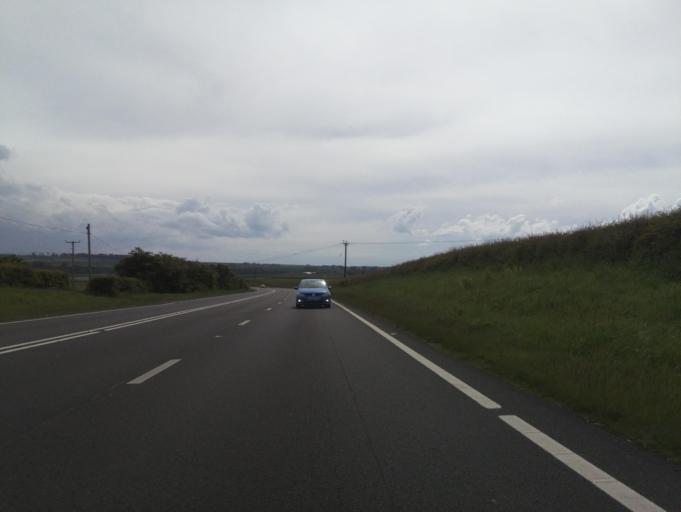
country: GB
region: England
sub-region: Northumberland
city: Berwick-Upon-Tweed
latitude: 55.7730
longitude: -2.0391
